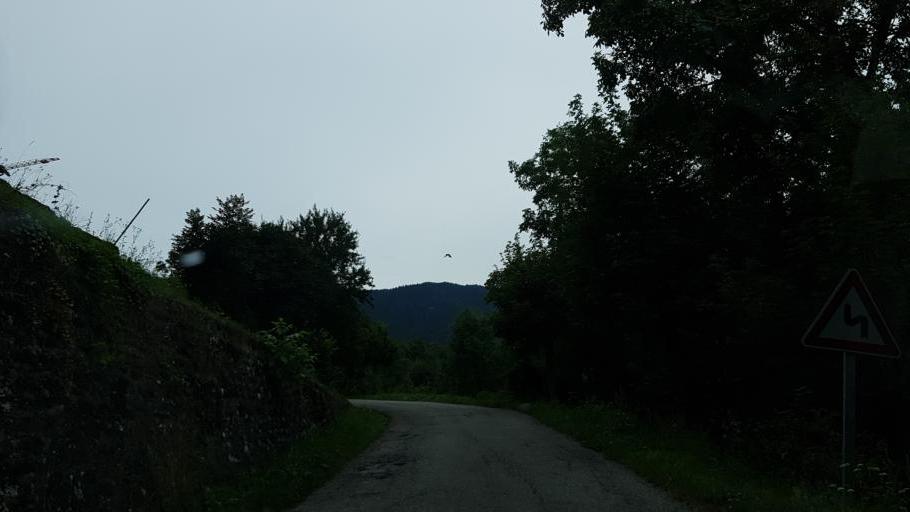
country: IT
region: Piedmont
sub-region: Provincia di Cuneo
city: Stroppo
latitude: 44.5081
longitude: 7.1243
